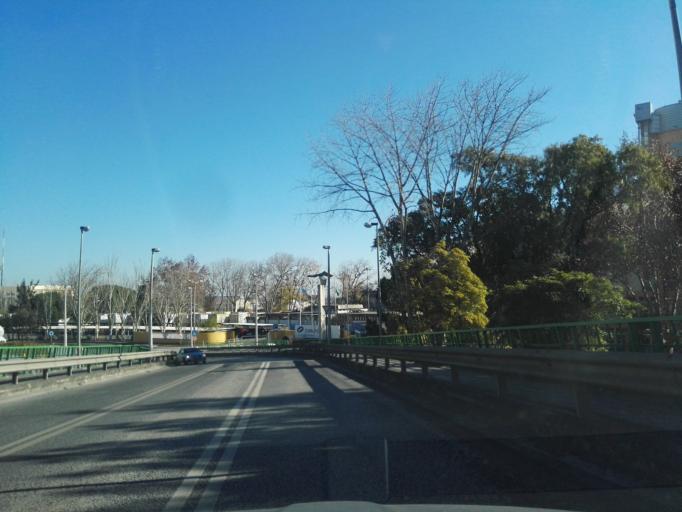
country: PT
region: Lisbon
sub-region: Vila Franca de Xira
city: Alhandra
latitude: 38.9243
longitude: -9.0103
